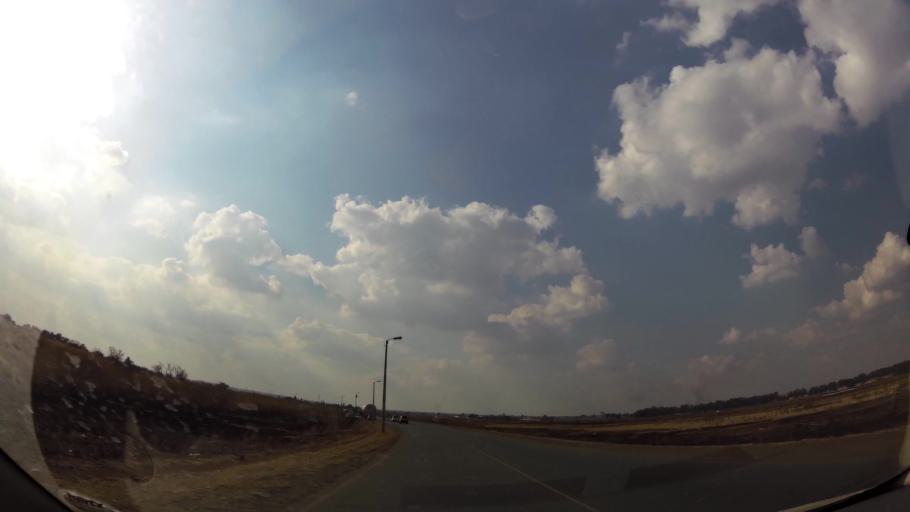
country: ZA
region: Gauteng
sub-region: Ekurhuleni Metropolitan Municipality
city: Germiston
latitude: -26.3006
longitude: 28.2128
